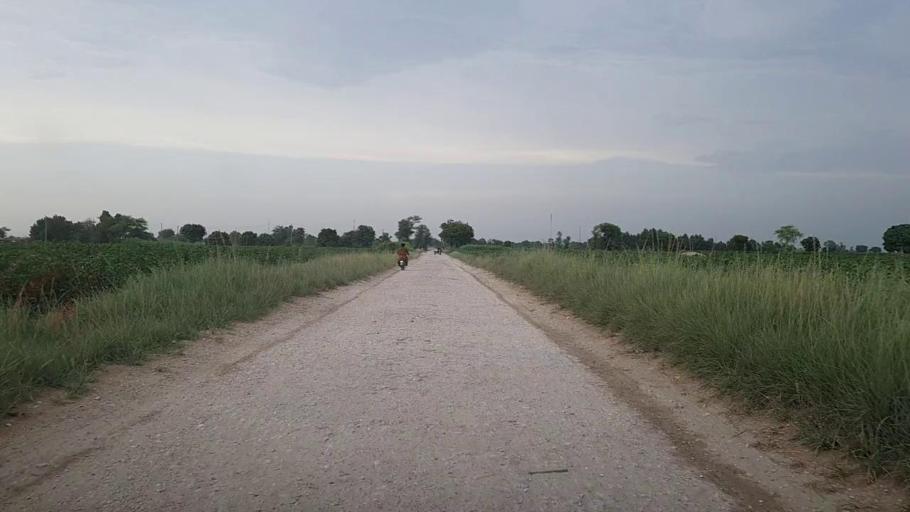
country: PK
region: Sindh
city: Karaundi
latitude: 26.9740
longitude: 68.3438
